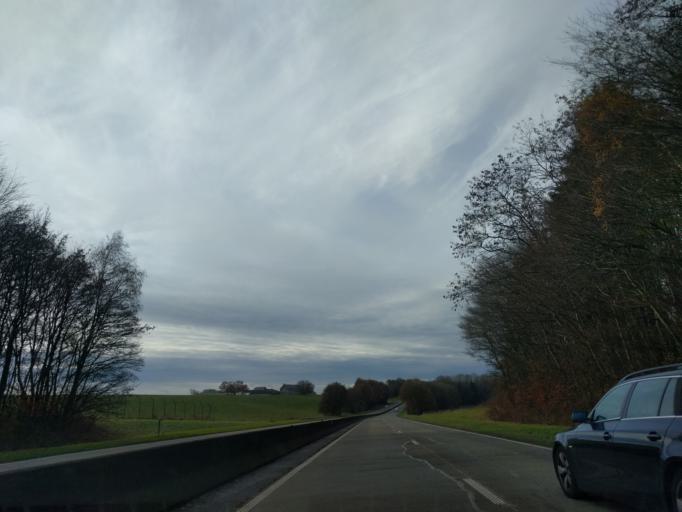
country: BE
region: Wallonia
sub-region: Province de Namur
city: Houyet
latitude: 50.2497
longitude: 5.0122
